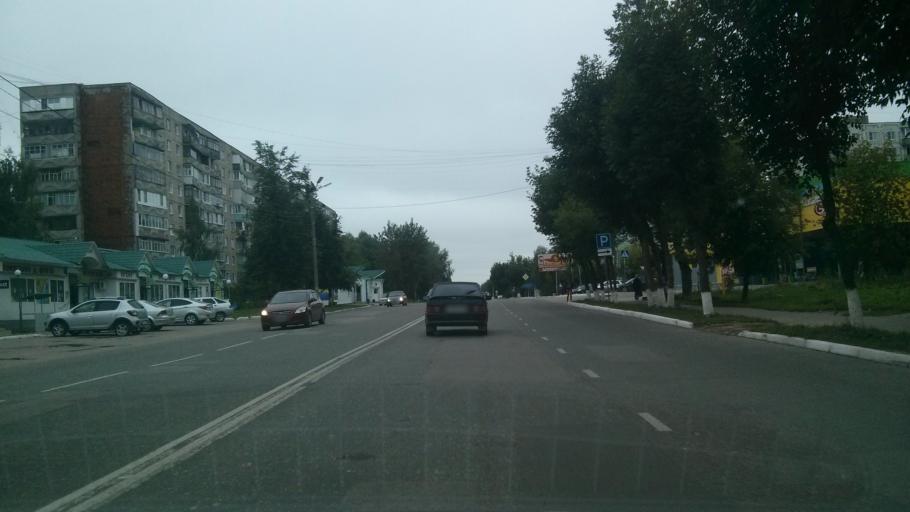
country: RU
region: Vladimir
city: Murom
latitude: 55.5668
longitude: 42.0614
